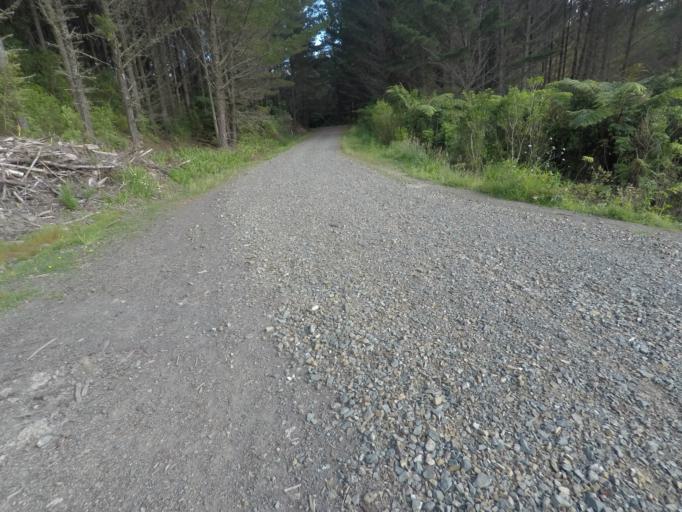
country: NZ
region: Auckland
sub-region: Auckland
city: Muriwai Beach
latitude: -36.7445
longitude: 174.5777
